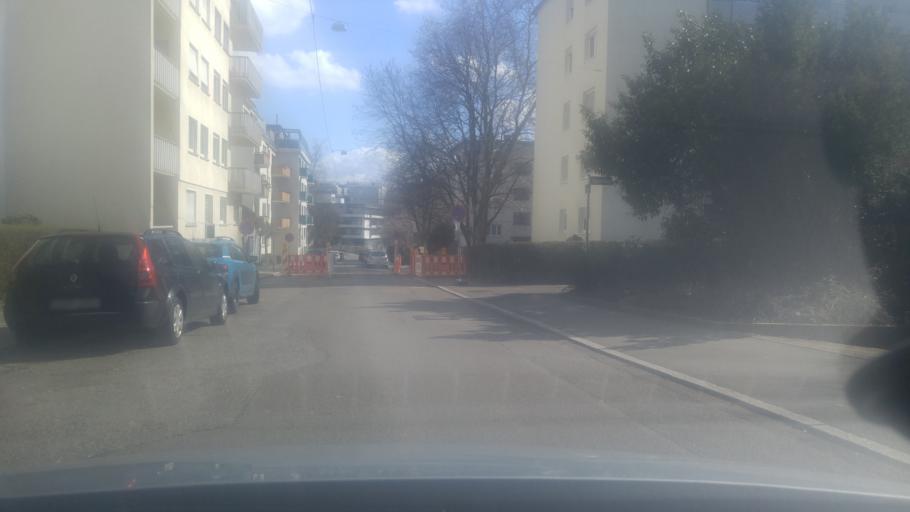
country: DE
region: Baden-Wuerttemberg
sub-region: Regierungsbezirk Stuttgart
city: Stuttgart
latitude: 48.7860
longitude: 9.1694
